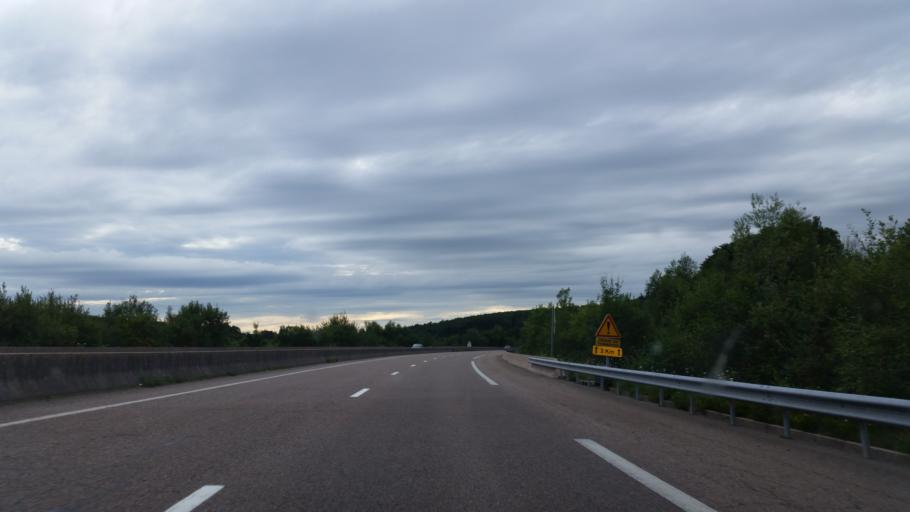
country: FR
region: Lorraine
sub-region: Departement des Vosges
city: Plombieres-les-Bains
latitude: 47.9864
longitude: 6.5174
